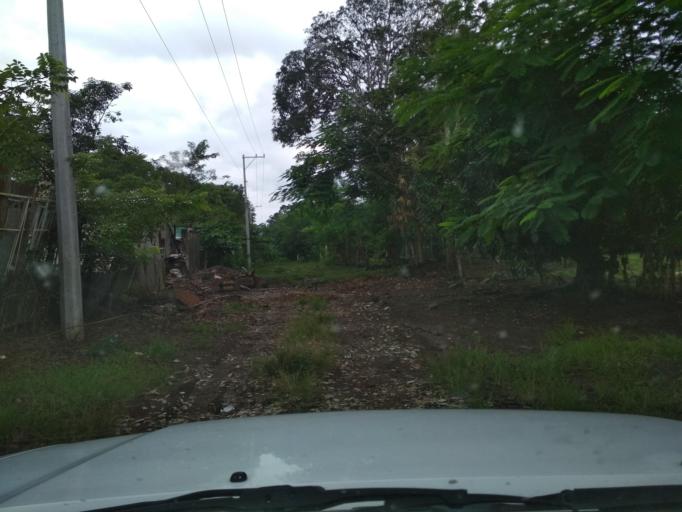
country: MX
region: Veracruz
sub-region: San Andres Tuxtla
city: El Huidero
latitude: 18.3917
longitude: -95.1954
